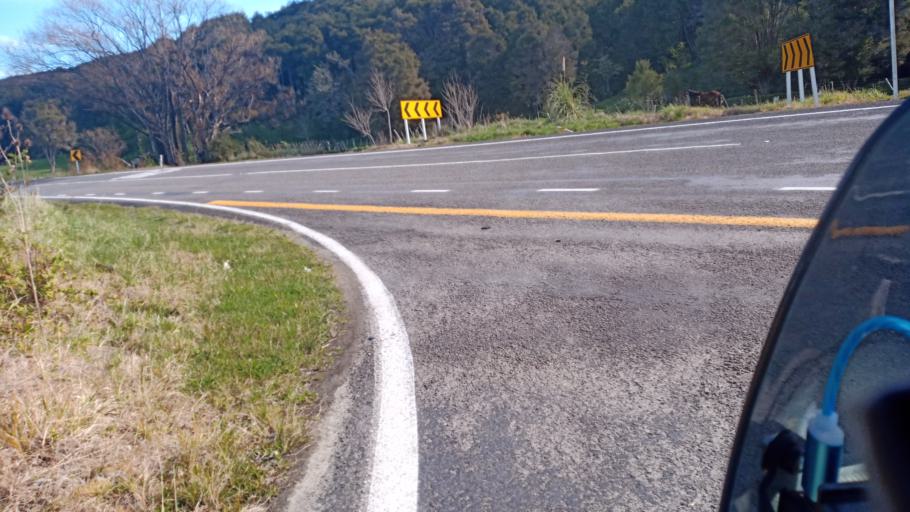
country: NZ
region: Gisborne
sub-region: Gisborne District
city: Gisborne
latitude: -37.9299
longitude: 178.2576
